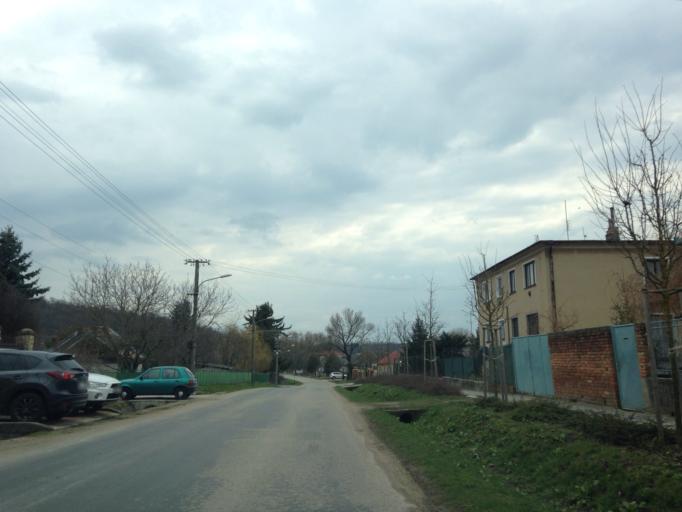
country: SK
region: Nitriansky
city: Svodin
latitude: 47.9565
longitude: 18.4120
